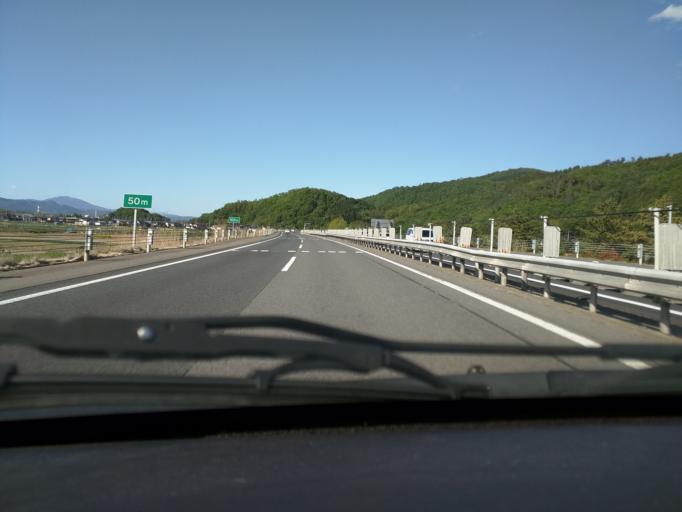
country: JP
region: Nagano
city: Nagano-shi
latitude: 36.5876
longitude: 138.2158
